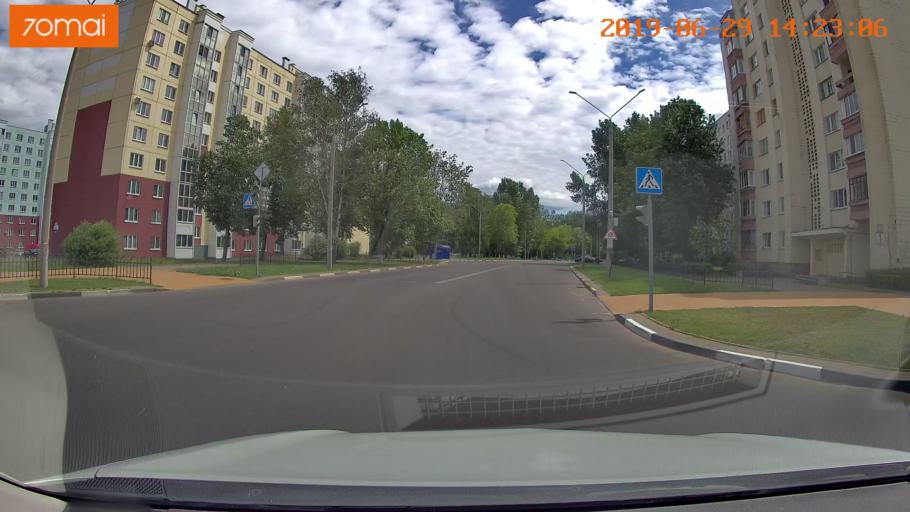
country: BY
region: Minsk
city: Salihorsk
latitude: 52.7879
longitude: 27.5533
